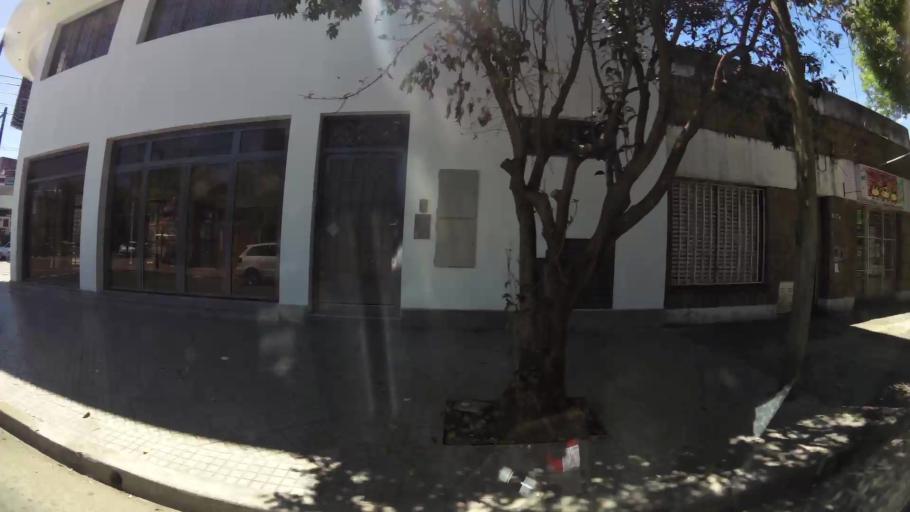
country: AR
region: Santa Fe
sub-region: Departamento de Rosario
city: Rosario
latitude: -32.9406
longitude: -60.7022
